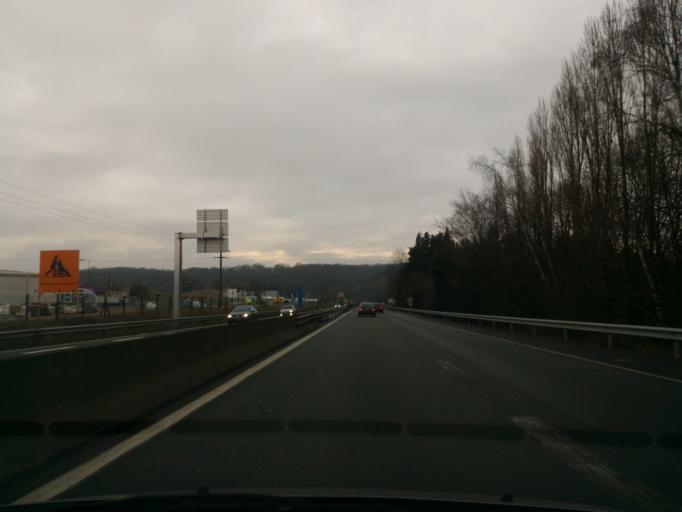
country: FR
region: Poitou-Charentes
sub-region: Departement de la Vienne
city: Fontaine-le-Comte
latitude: 46.5307
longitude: 0.2829
